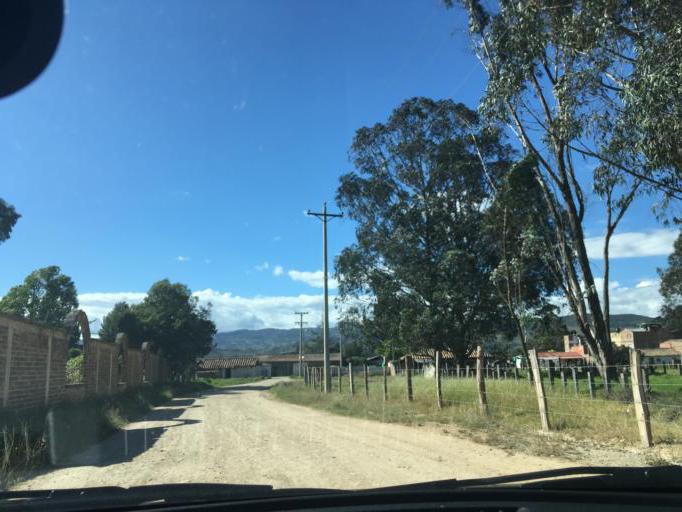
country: CO
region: Boyaca
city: Firavitoba
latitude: 5.6745
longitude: -72.9591
